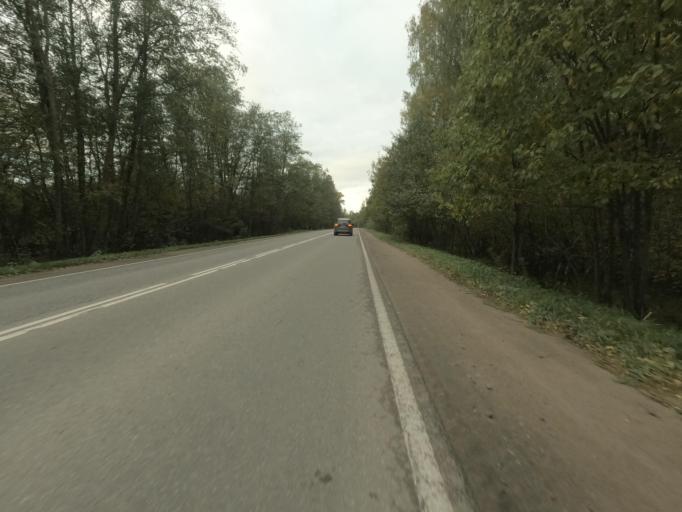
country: RU
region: Leningrad
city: Pavlovo
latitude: 59.7840
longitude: 30.9700
